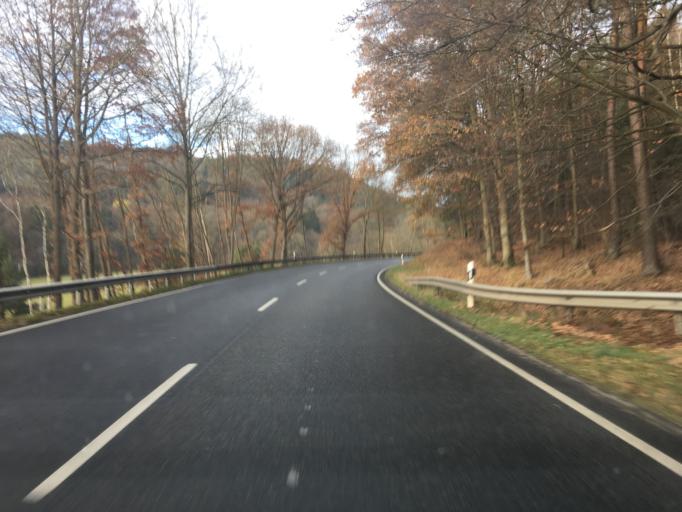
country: DE
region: North Rhine-Westphalia
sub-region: Regierungsbezirk Koln
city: Kall
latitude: 50.5612
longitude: 6.5363
